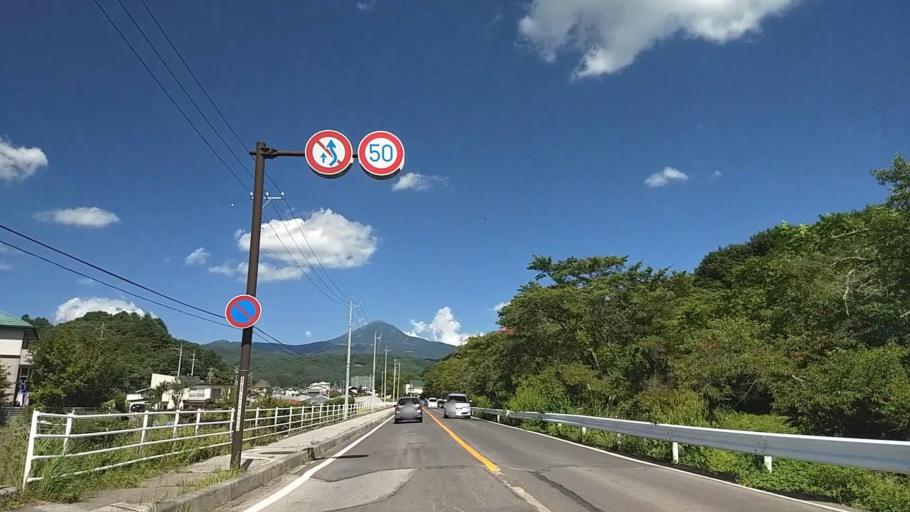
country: JP
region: Nagano
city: Chino
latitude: 36.0241
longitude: 138.1782
